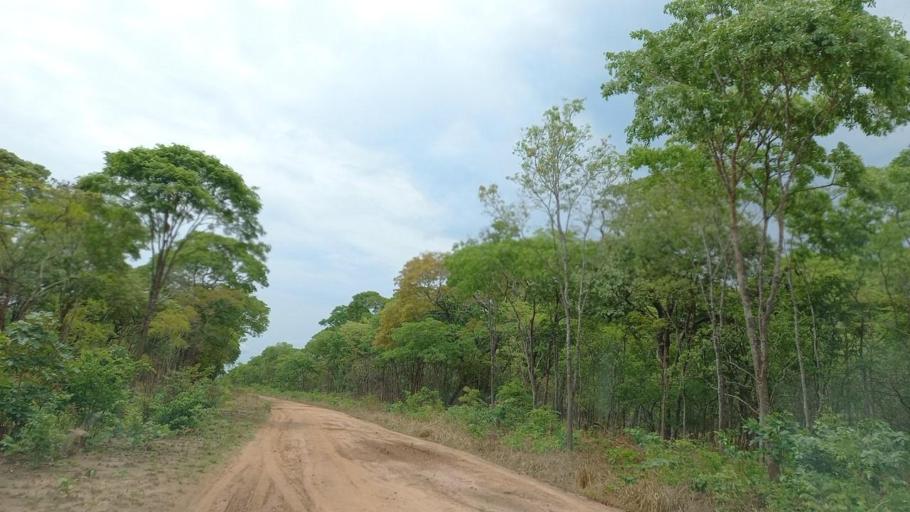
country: ZM
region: North-Western
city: Kalengwa
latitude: -13.5706
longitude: 24.9705
